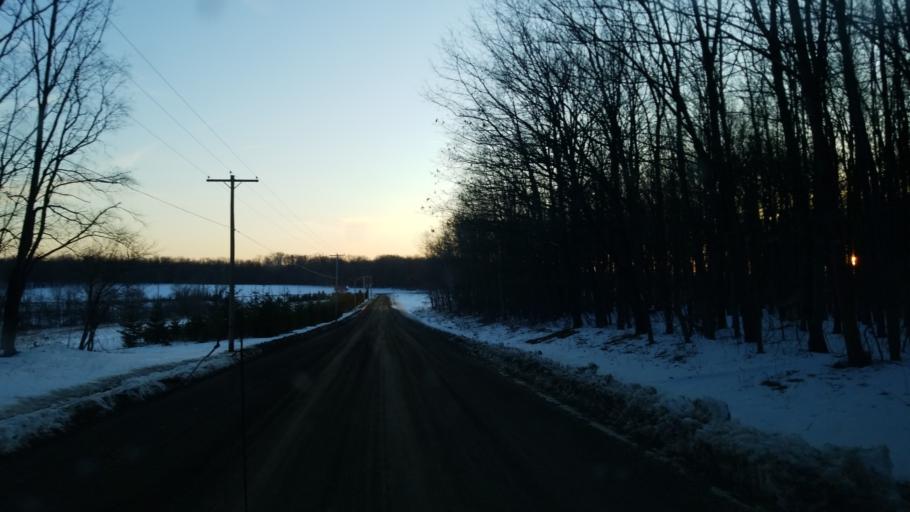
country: US
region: Pennsylvania
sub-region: Tioga County
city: Westfield
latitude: 42.0041
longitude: -77.6870
